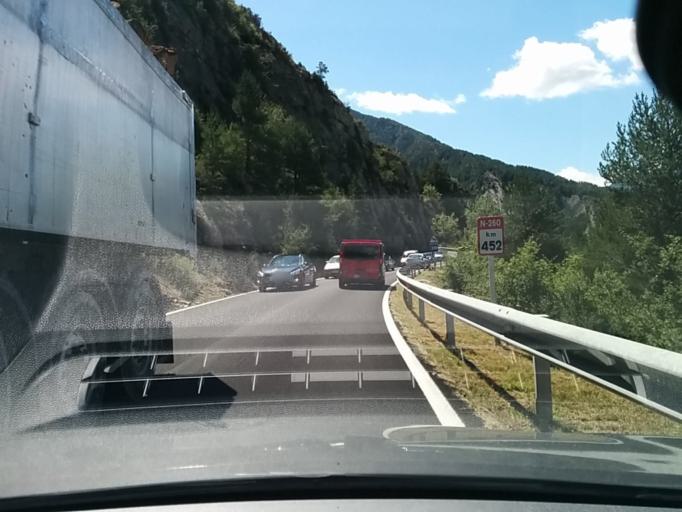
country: ES
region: Aragon
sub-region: Provincia de Huesca
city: Boltana
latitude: 42.4705
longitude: -0.0005
